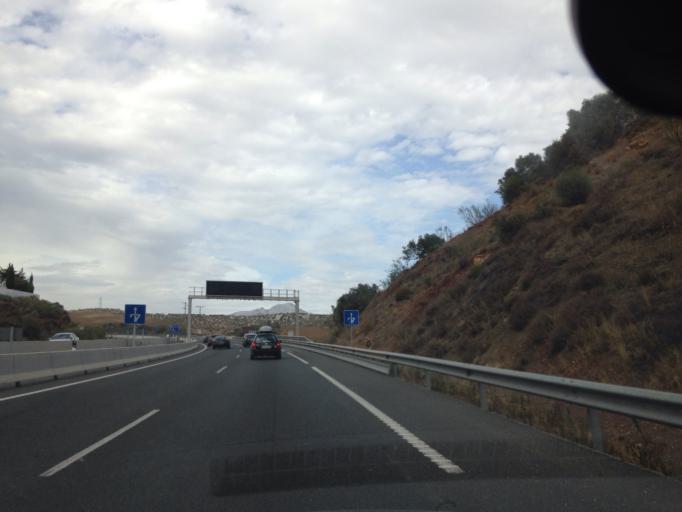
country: ES
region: Andalusia
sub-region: Provincia de Malaga
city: Casabermeja
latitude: 36.8945
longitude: -4.4228
